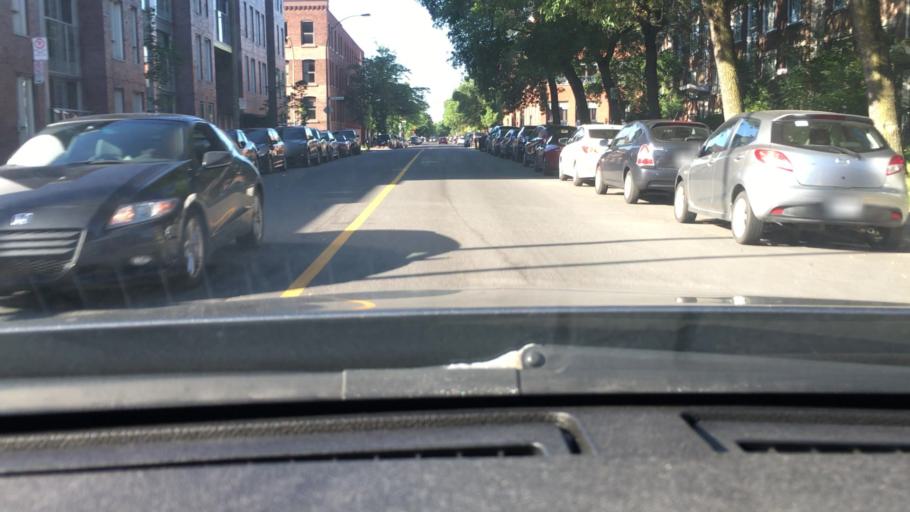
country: CA
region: Quebec
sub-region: Monteregie
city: Longueuil
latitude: 45.5536
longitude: -73.5434
